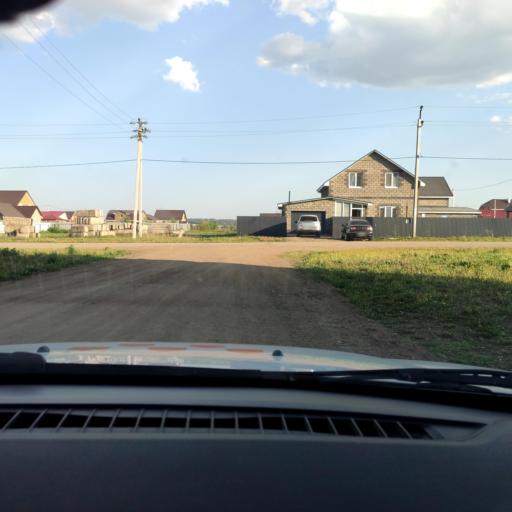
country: RU
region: Bashkortostan
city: Karmaskaly
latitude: 54.3535
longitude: 56.1447
